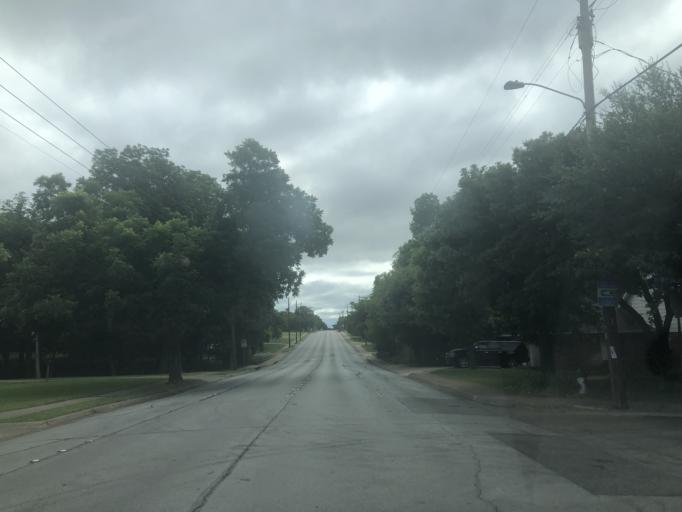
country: US
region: Texas
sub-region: Dallas County
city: Duncanville
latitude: 32.6517
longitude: -96.9203
